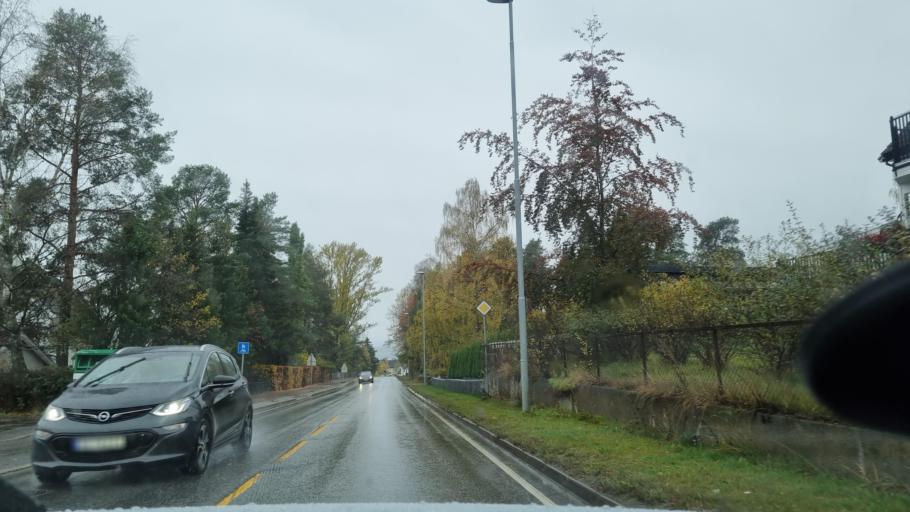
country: NO
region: Hedmark
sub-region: Hamar
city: Hamar
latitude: 60.8095
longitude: 11.0561
